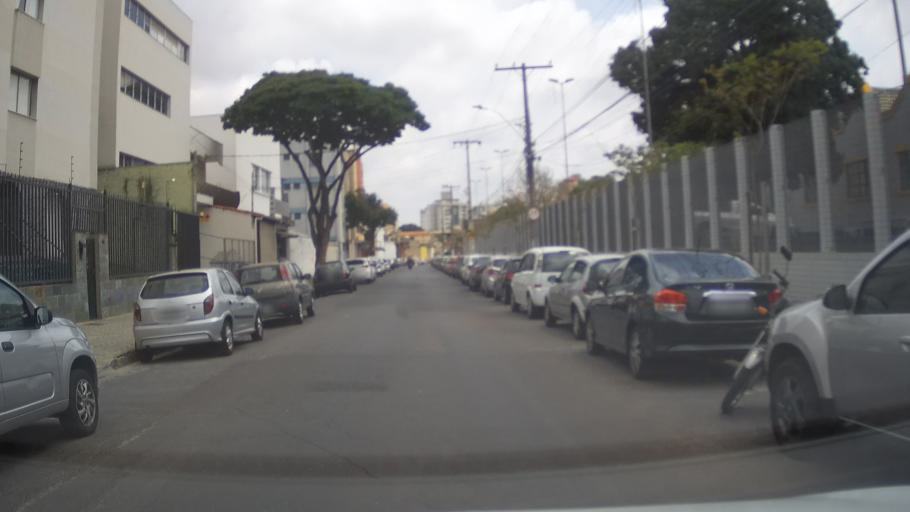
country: BR
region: Minas Gerais
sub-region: Belo Horizonte
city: Belo Horizonte
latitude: -19.8919
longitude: -43.9358
